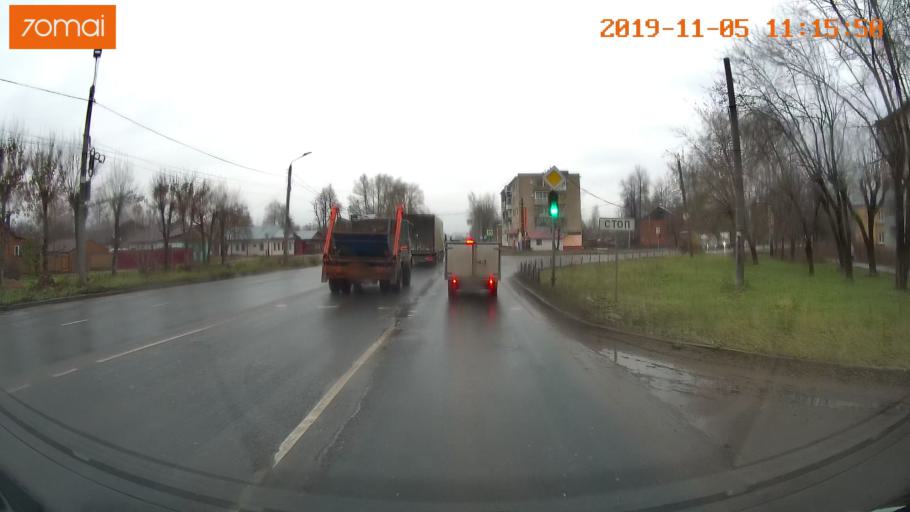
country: RU
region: Ivanovo
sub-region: Gorod Ivanovo
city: Ivanovo
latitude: 56.9801
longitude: 40.9539
